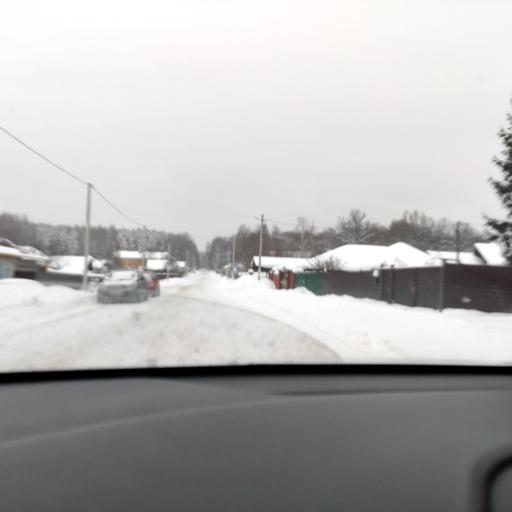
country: RU
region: Tatarstan
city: Vysokaya Gora
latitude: 55.9557
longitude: 49.1593
